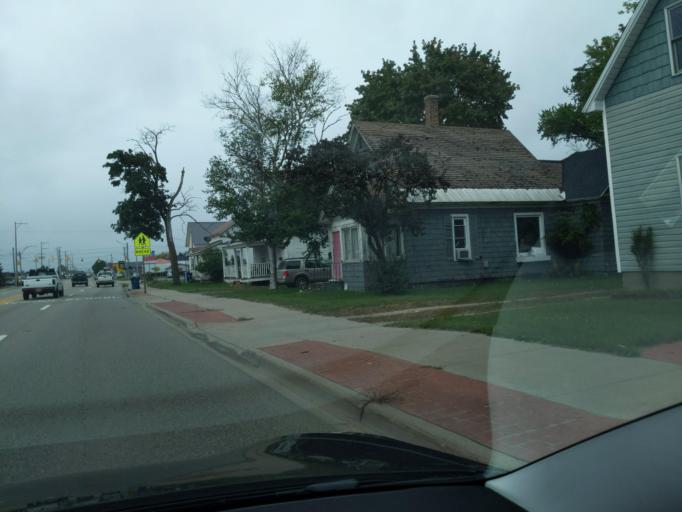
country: US
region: Michigan
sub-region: Wexford County
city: Cadillac
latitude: 44.2598
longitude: -85.4051
